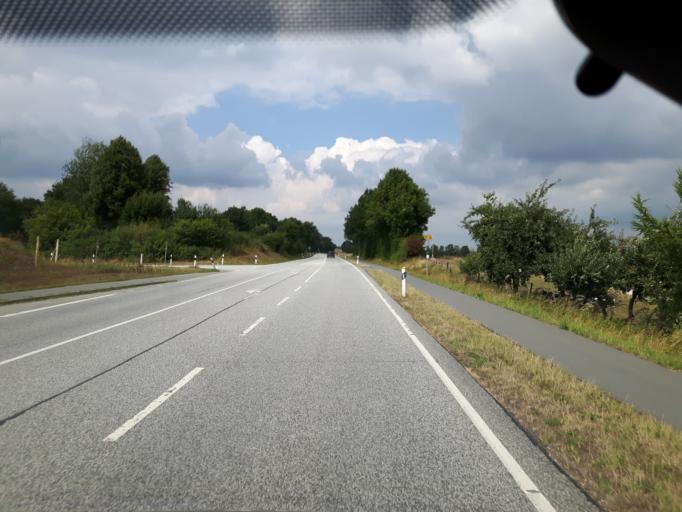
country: DE
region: Schleswig-Holstein
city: Holzbunge
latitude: 54.3647
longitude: 9.7044
